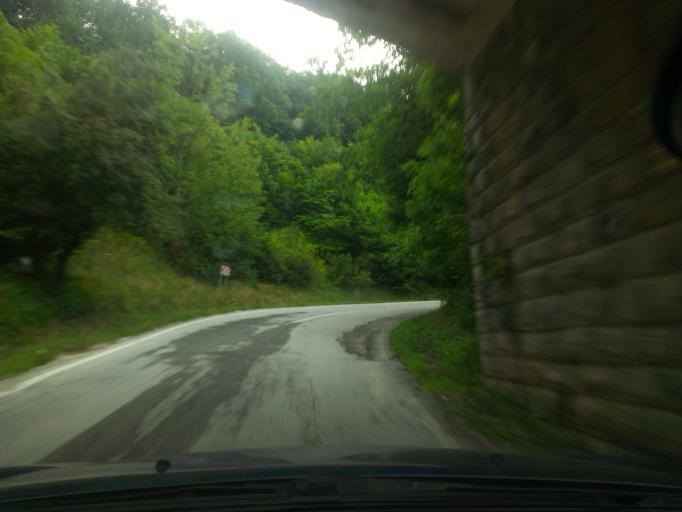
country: CZ
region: South Moravian
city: Velka nad Velickou
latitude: 48.8123
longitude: 17.5201
